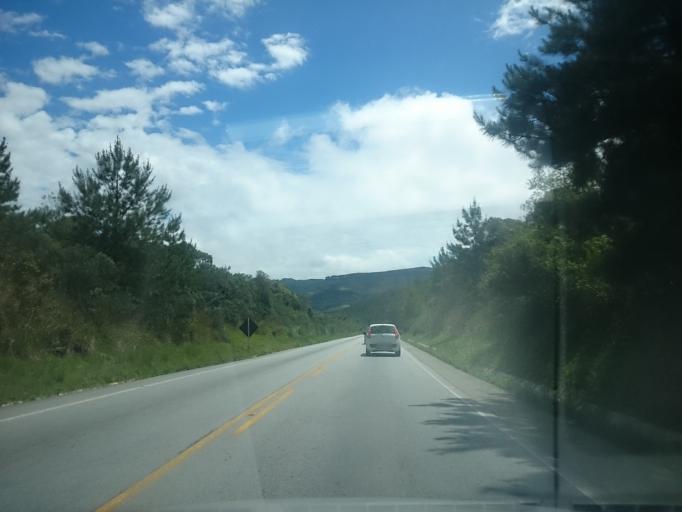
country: BR
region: Santa Catarina
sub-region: Anitapolis
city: Anitapolis
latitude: -27.6678
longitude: -49.1765
